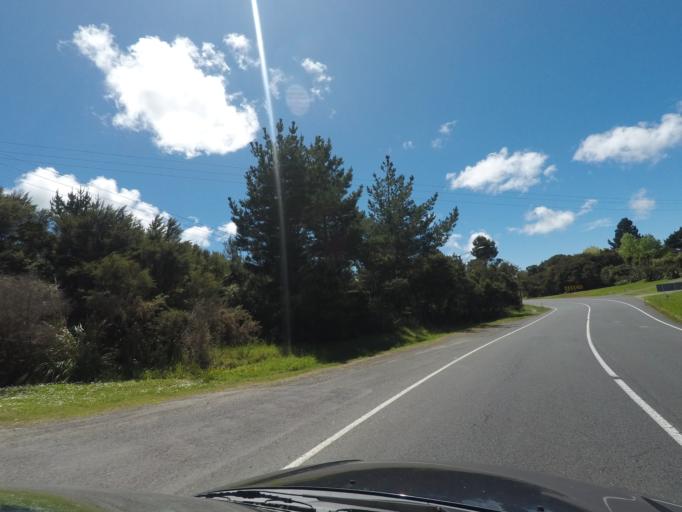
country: NZ
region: Auckland
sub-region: Auckland
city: Rothesay Bay
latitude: -36.7520
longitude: 174.6672
